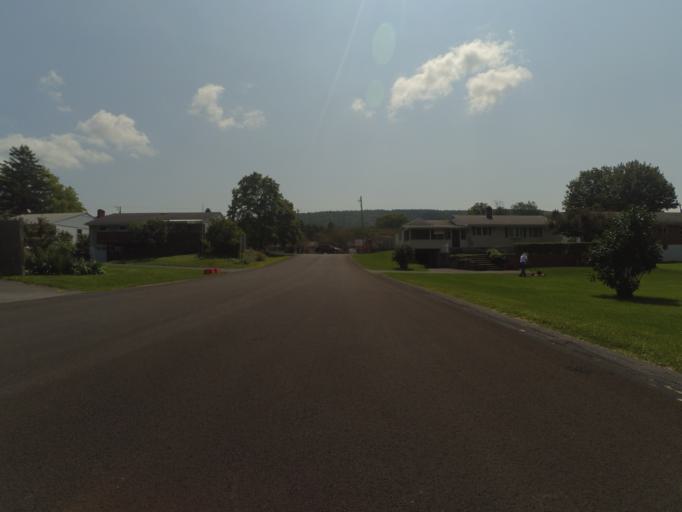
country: US
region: Pennsylvania
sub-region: Centre County
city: Pleasant Gap
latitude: 40.8648
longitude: -77.7522
